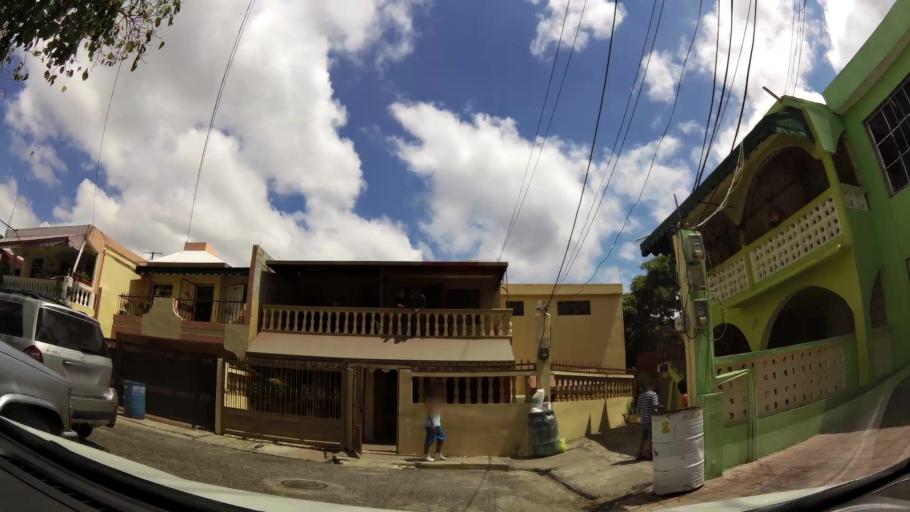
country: DO
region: Nacional
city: Bella Vista
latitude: 18.4328
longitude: -69.9583
